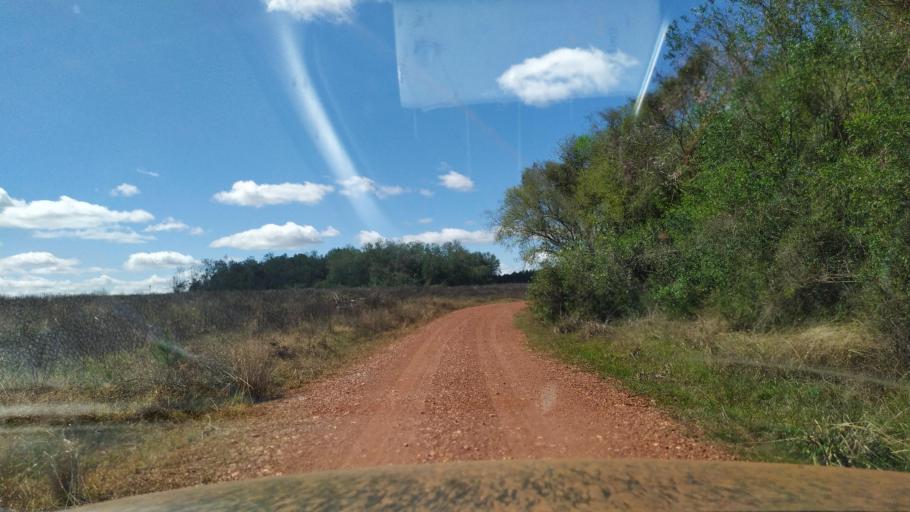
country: AR
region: Corrientes
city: Gobernador Ingeniero Valentin Virasoro
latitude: -28.2904
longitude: -56.0503
